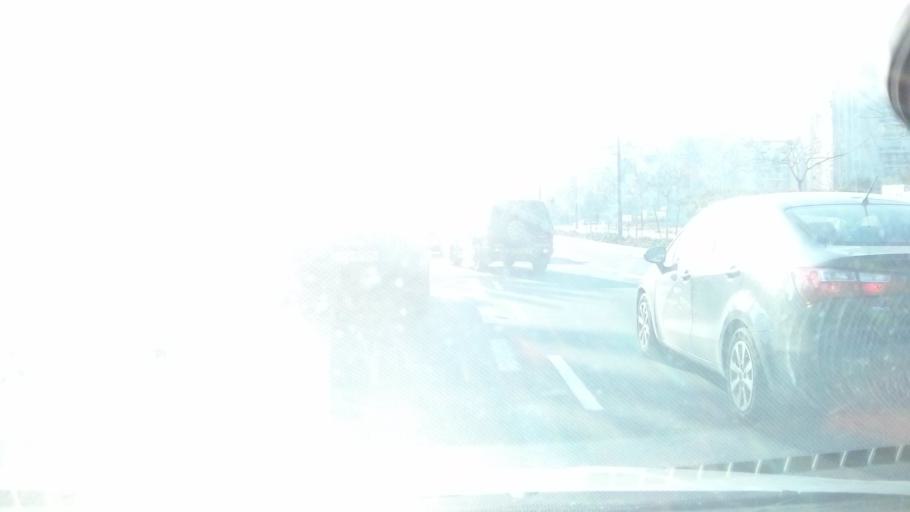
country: IL
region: Central District
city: Even Yehuda
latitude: 32.2793
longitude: 34.8487
